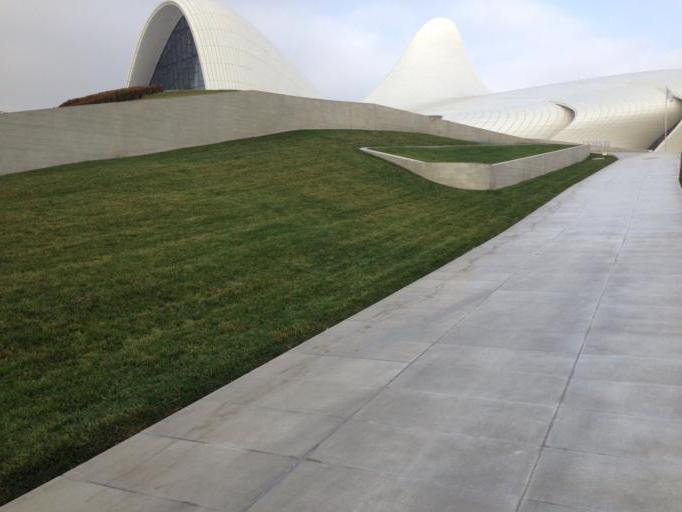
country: AZ
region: Baki
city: Baku
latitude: 40.3942
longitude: 49.8677
